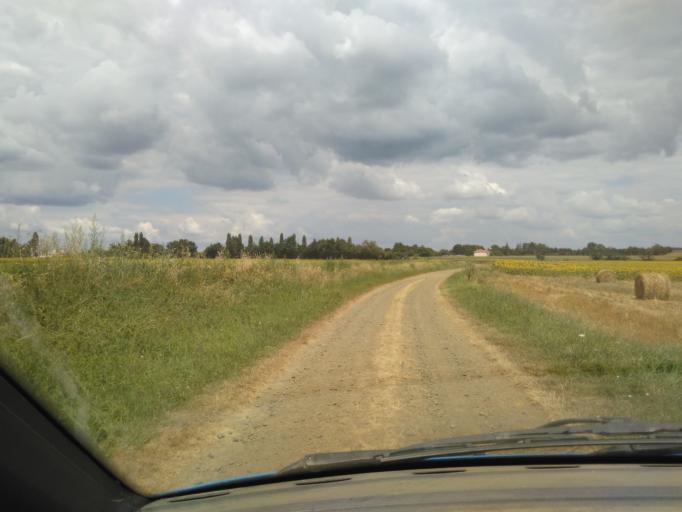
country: FR
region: Pays de la Loire
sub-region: Departement de la Vendee
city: Sainte-Hermine
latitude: 46.5729
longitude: -1.0243
